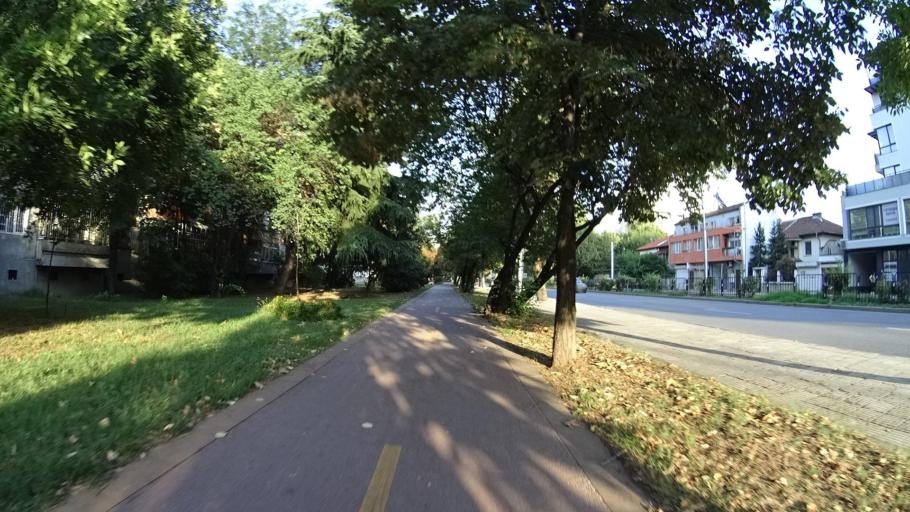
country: BG
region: Plovdiv
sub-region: Obshtina Plovdiv
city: Plovdiv
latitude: 42.1272
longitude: 24.7308
